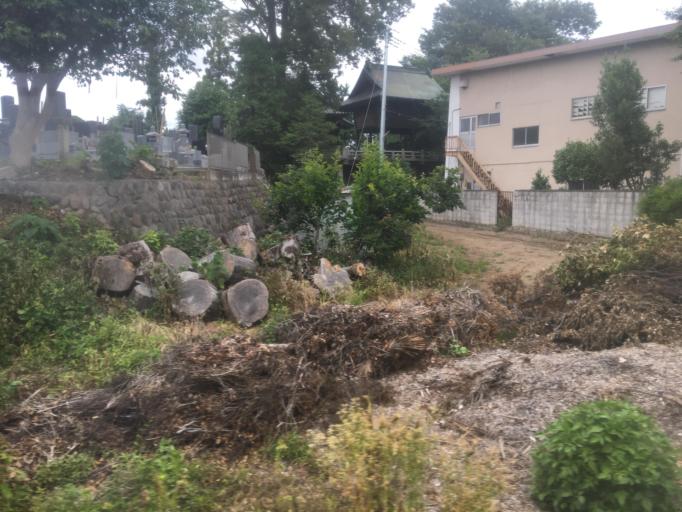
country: JP
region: Gunma
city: Takasaki
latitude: 36.3096
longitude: 139.0129
